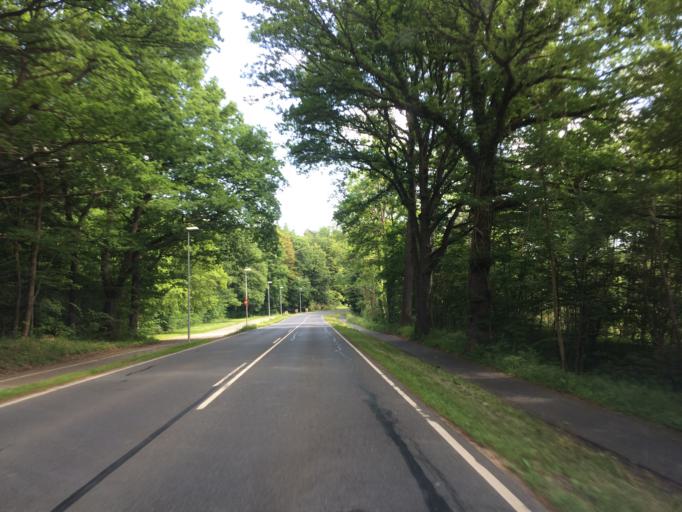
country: DK
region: Central Jutland
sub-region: Silkeborg Kommune
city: Silkeborg
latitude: 56.1611
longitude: 9.5185
